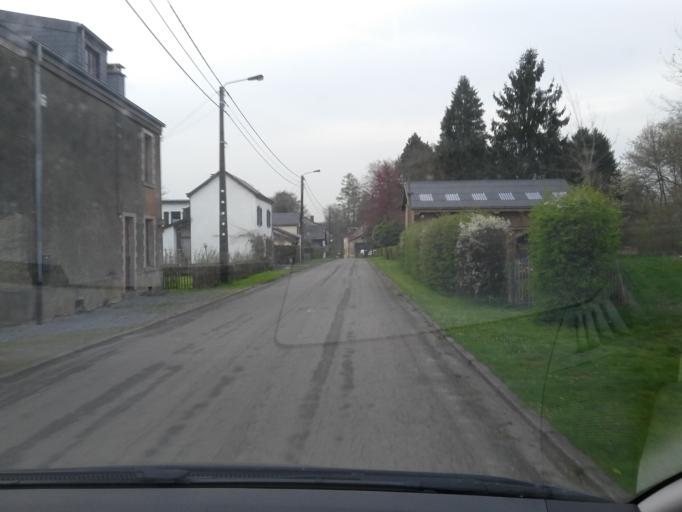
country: BE
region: Wallonia
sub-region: Province du Luxembourg
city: Herbeumont
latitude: 49.7837
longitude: 5.2332
